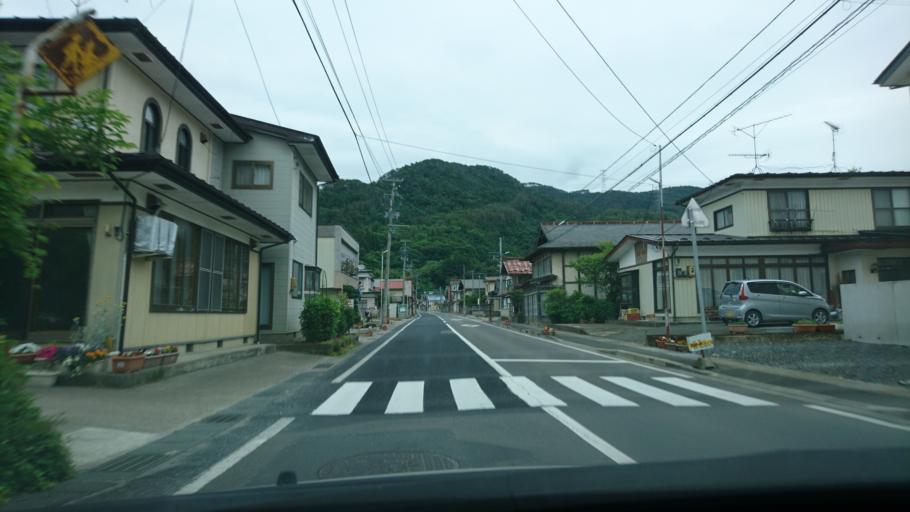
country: JP
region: Iwate
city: Ichinoseki
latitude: 38.9545
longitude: 141.2548
